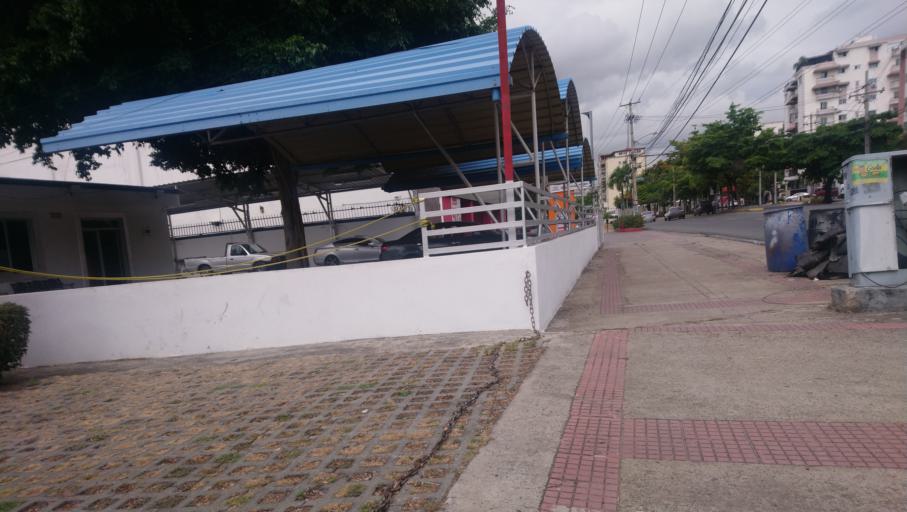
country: DO
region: Nacional
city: Ciudad Nueva
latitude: 18.4679
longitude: -69.9078
